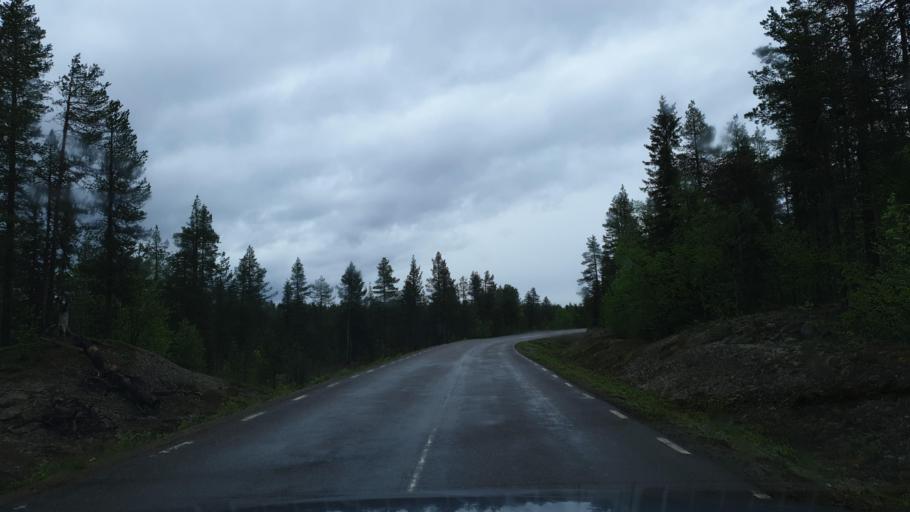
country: SE
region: Norrbotten
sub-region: Gallivare Kommun
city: Malmberget
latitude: 67.8921
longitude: 21.0458
